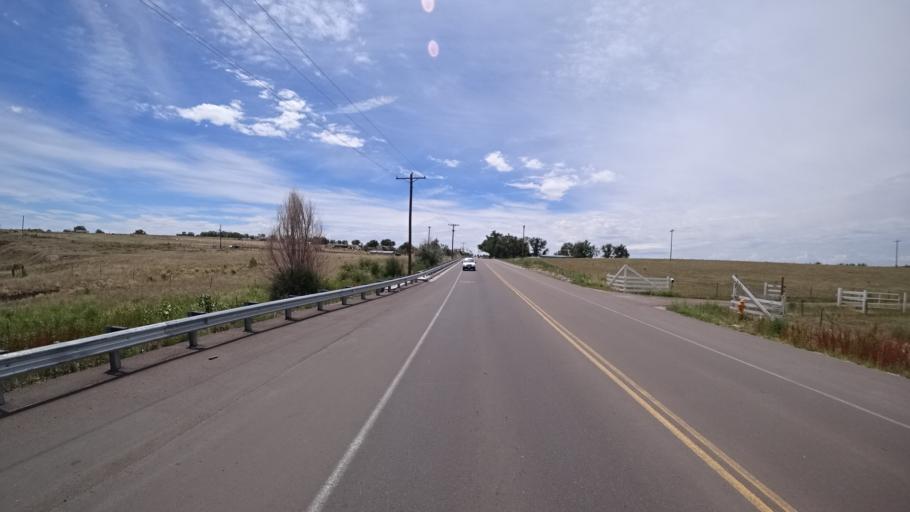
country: US
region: Colorado
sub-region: El Paso County
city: Fountain
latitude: 38.7002
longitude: -104.6736
